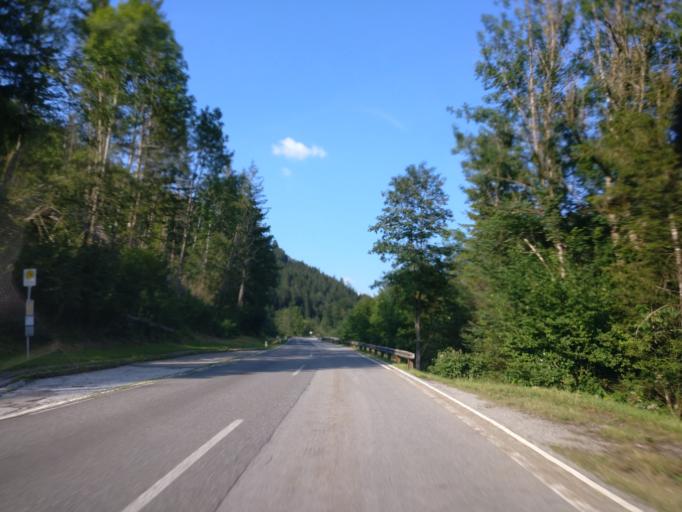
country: AT
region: Styria
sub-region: Politischer Bezirk Liezen
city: Palfau
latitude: 47.7308
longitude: 14.8673
